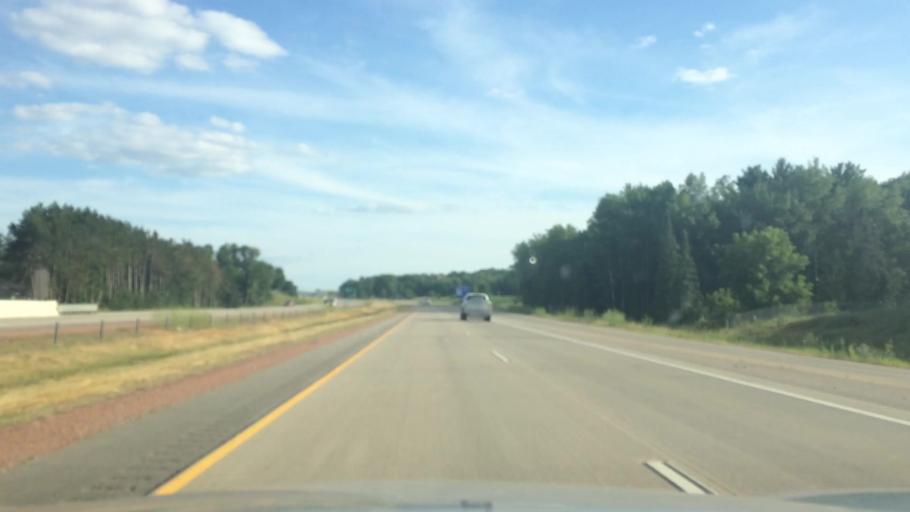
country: US
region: Wisconsin
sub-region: Marathon County
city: Wausau
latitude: 44.9837
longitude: -89.6574
